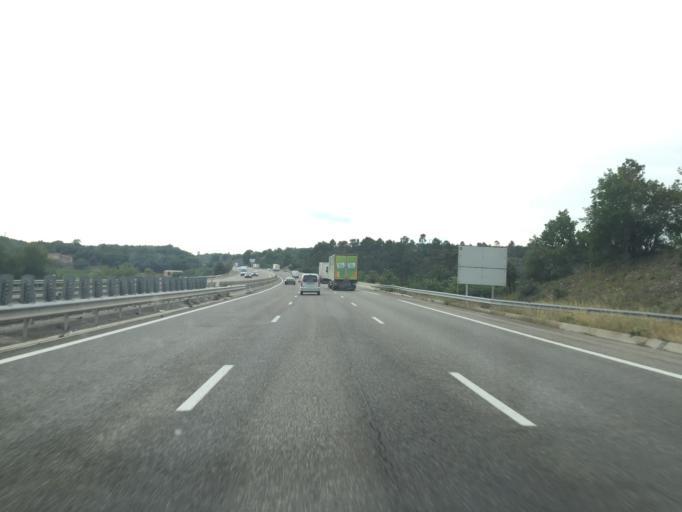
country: FR
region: Provence-Alpes-Cote d'Azur
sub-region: Departement du Var
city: Tourves
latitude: 43.4417
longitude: 5.9040
